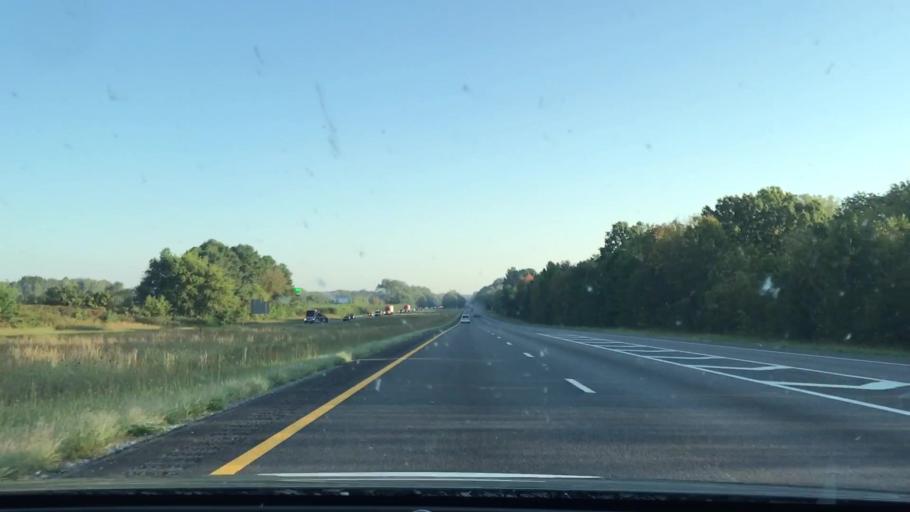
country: US
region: Tennessee
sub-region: Sumner County
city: White House
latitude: 36.4726
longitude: -86.6805
